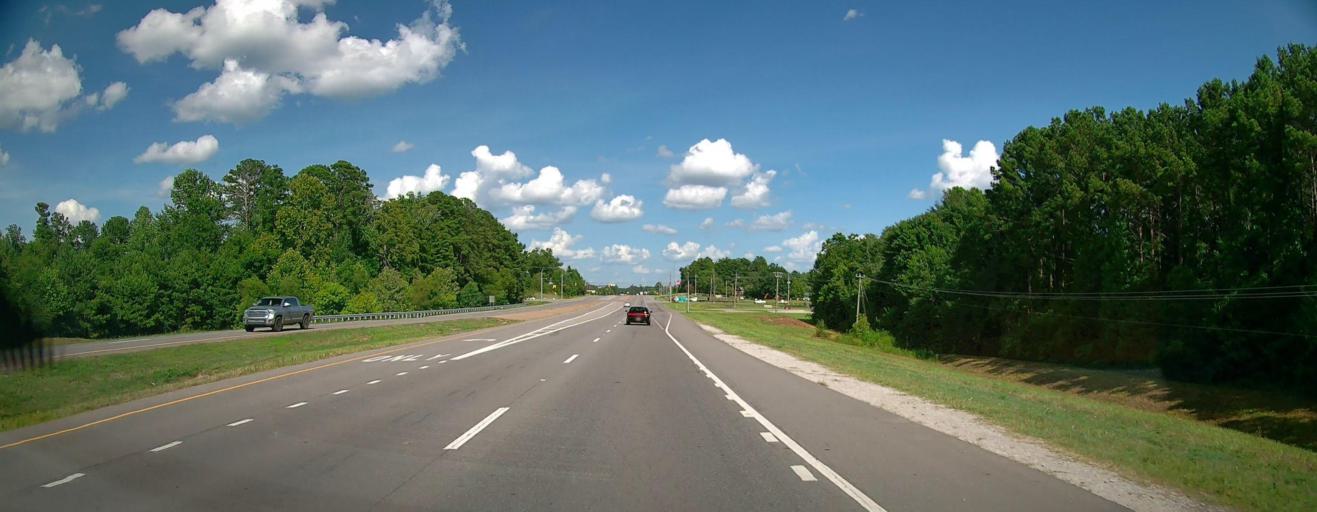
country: US
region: Alabama
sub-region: Tuscaloosa County
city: Northport
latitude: 33.2347
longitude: -87.6422
